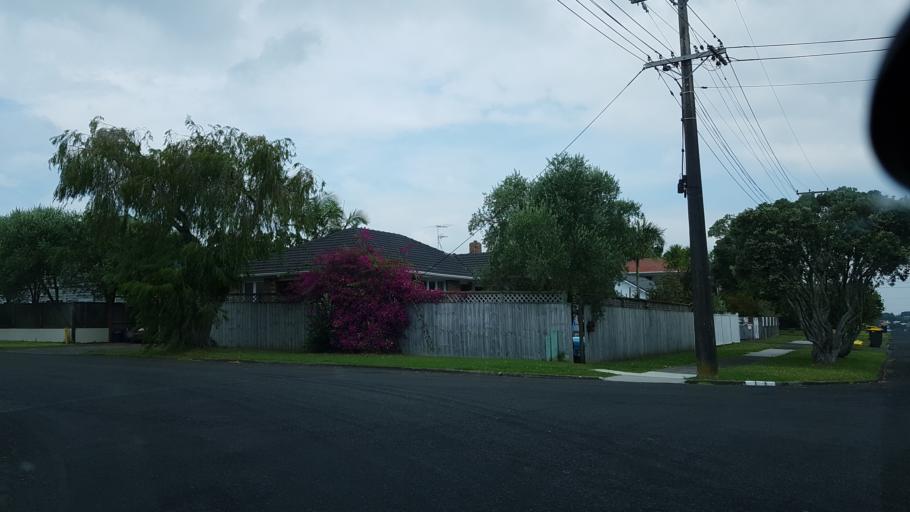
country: NZ
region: Auckland
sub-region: Auckland
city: North Shore
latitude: -36.8064
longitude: 174.7816
